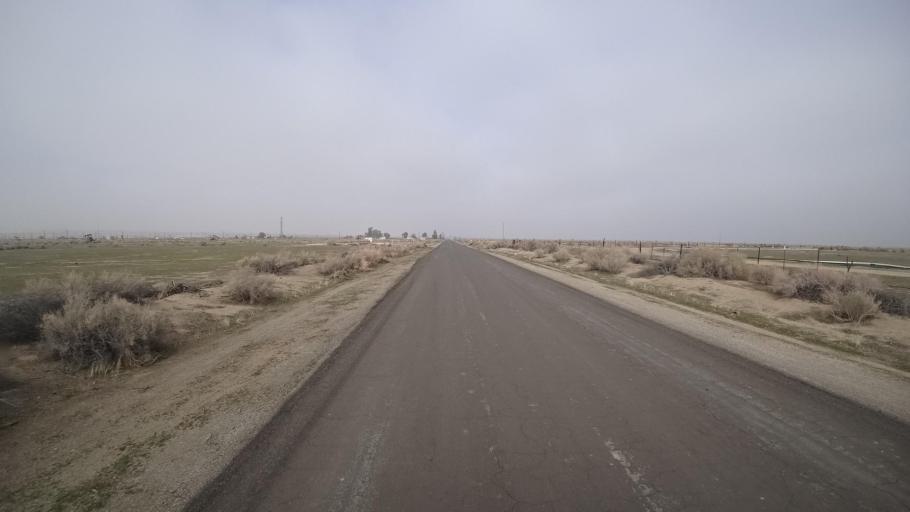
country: US
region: California
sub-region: Kern County
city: Maricopa
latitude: 35.0511
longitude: -119.3492
